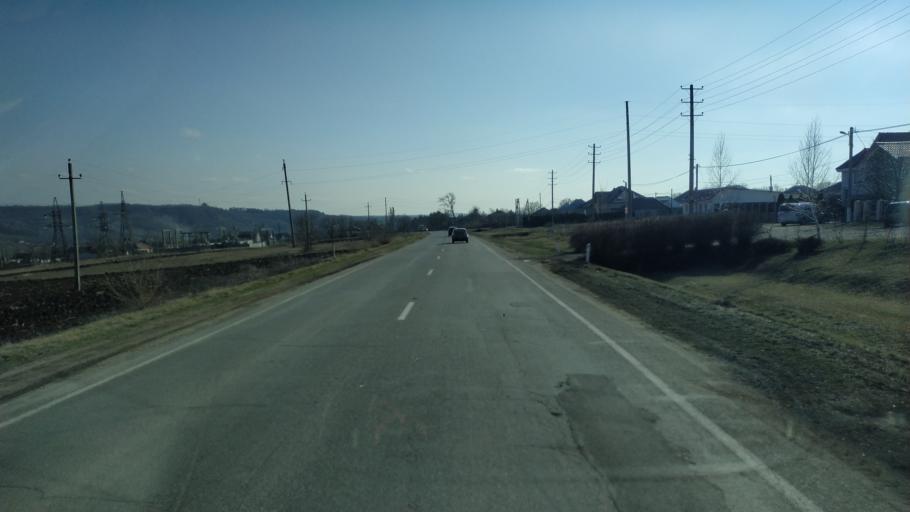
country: MD
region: Hincesti
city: Hincesti
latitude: 46.7496
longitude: 28.5213
